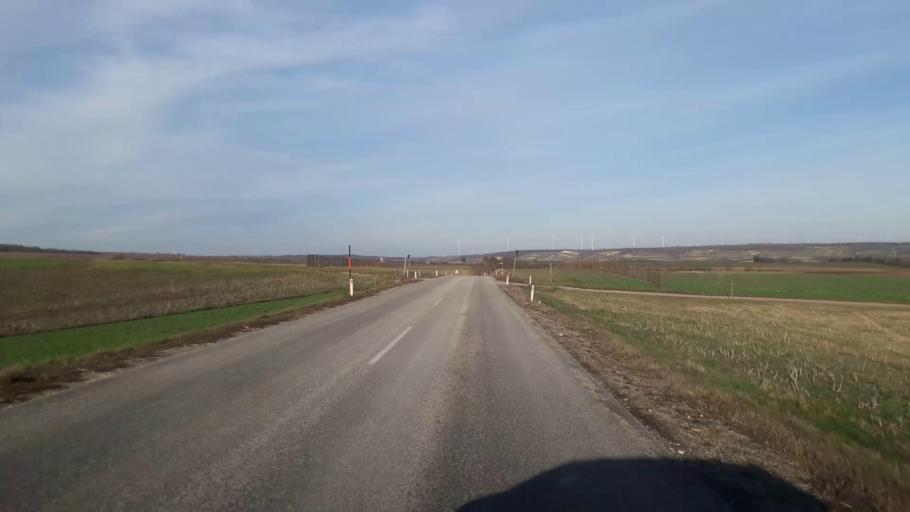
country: AT
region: Lower Austria
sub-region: Politischer Bezirk Ganserndorf
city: Auersthal
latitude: 48.3836
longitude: 16.6303
